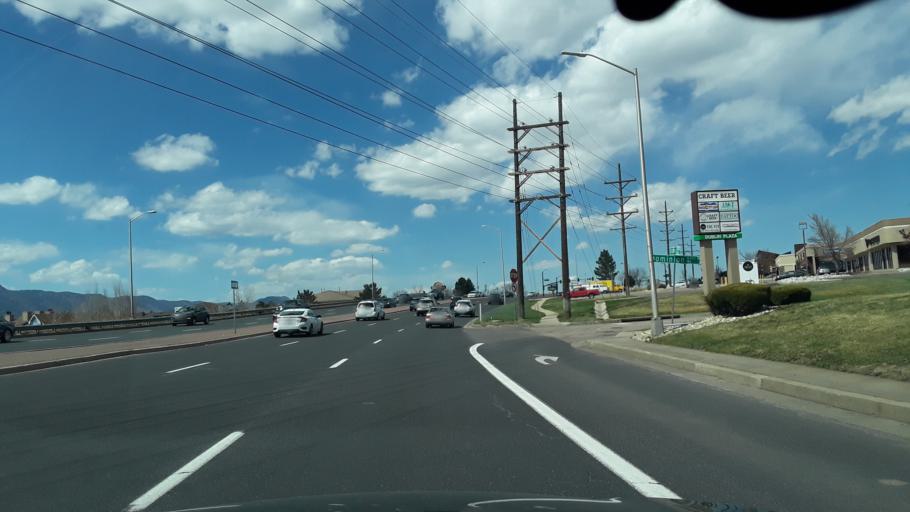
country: US
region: Colorado
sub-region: El Paso County
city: Colorado Springs
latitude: 38.9232
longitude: -104.7935
